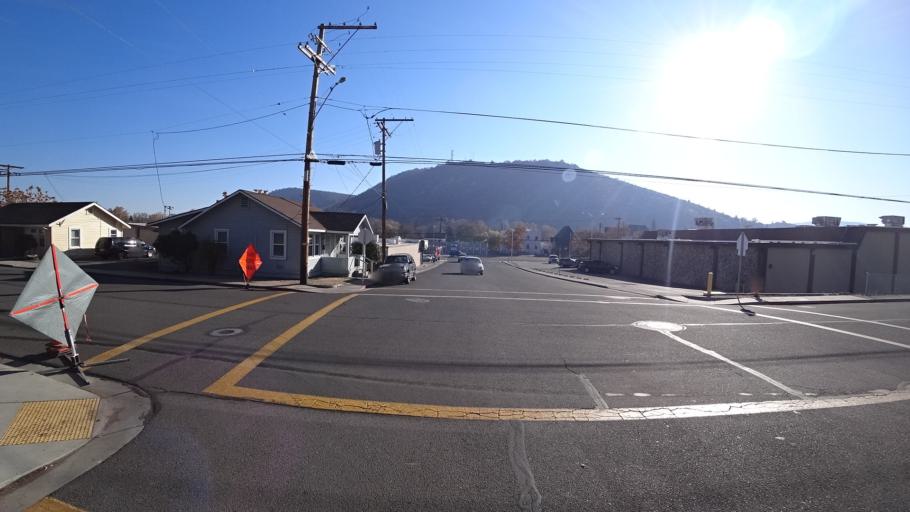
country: US
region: California
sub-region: Siskiyou County
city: Yreka
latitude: 41.7264
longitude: -122.6396
